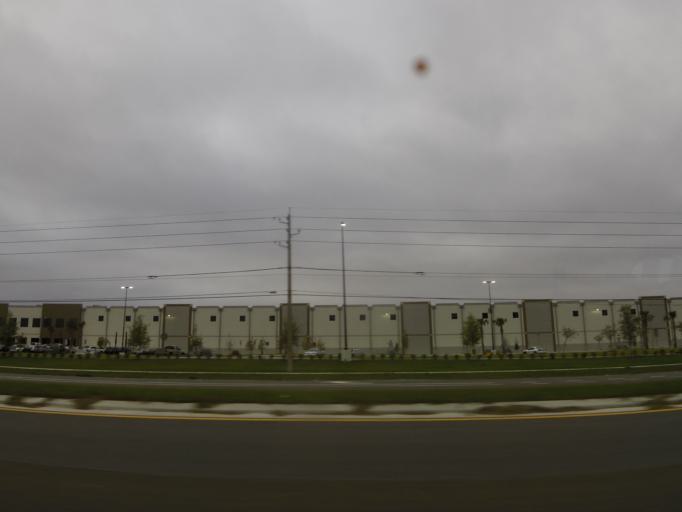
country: US
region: Florida
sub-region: Duval County
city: Baldwin
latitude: 30.2462
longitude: -81.8627
